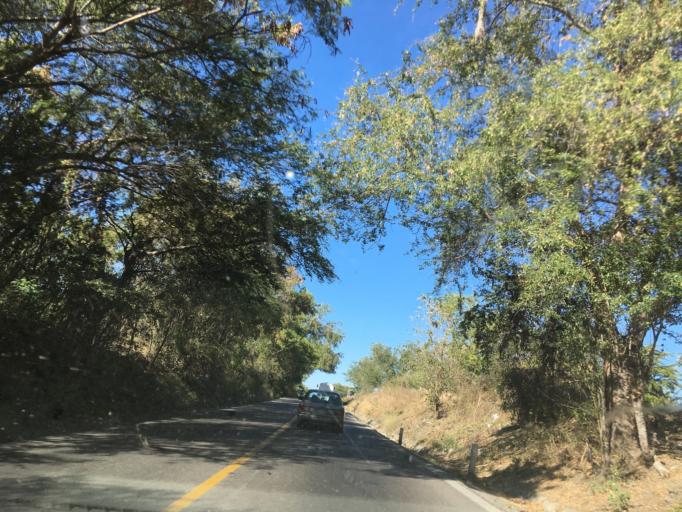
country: MX
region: Michoacan
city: Nueva Italia de Ruiz
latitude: 19.0860
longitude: -102.0589
